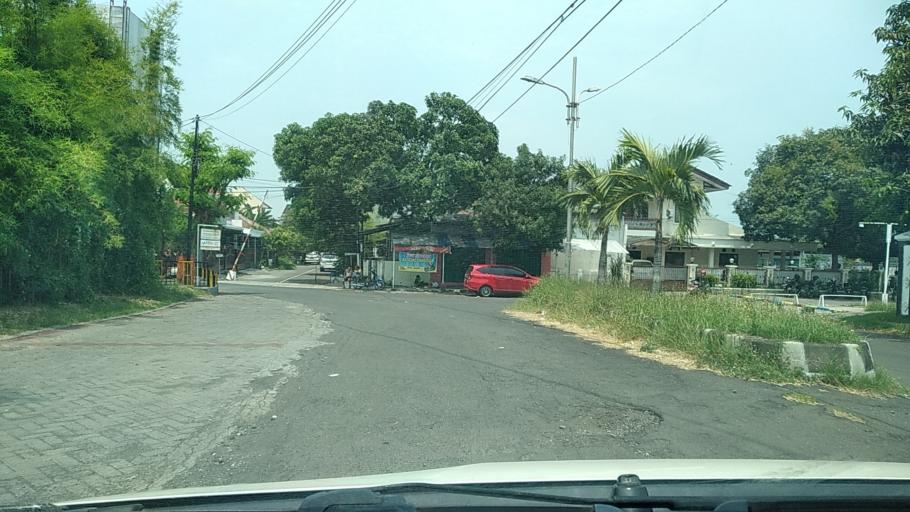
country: ID
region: Central Java
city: Semarang
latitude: -6.9817
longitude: 110.3659
